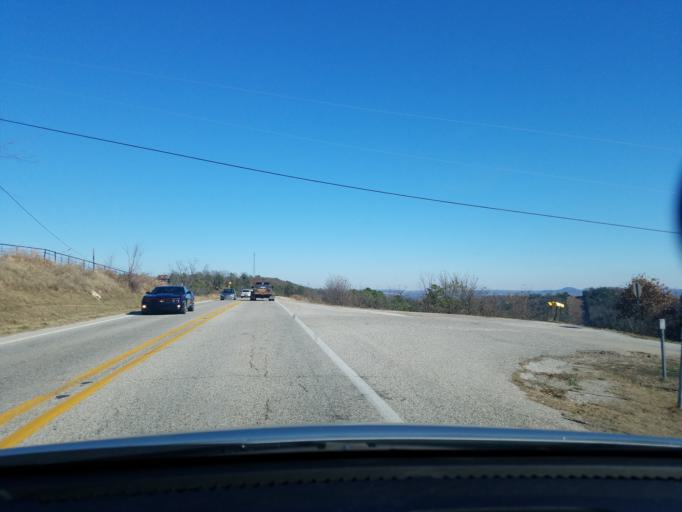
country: US
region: Arkansas
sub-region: Carroll County
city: Eureka Springs
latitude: 36.3965
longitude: -93.6898
